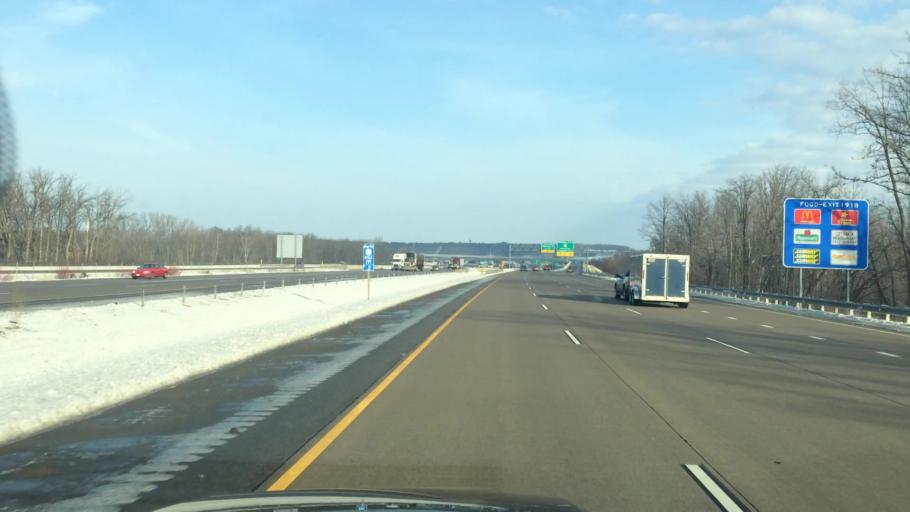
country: US
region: Wisconsin
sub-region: Marathon County
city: Rib Mountain
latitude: 44.9423
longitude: -89.6664
